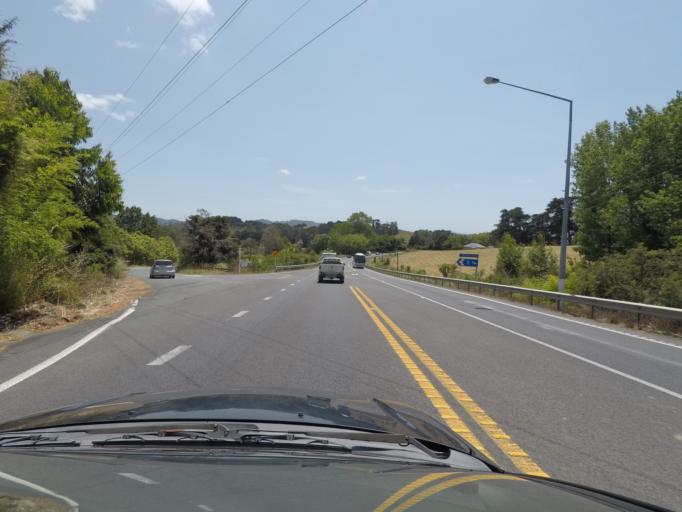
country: NZ
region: Auckland
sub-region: Auckland
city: Warkworth
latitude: -36.4247
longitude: 174.6465
